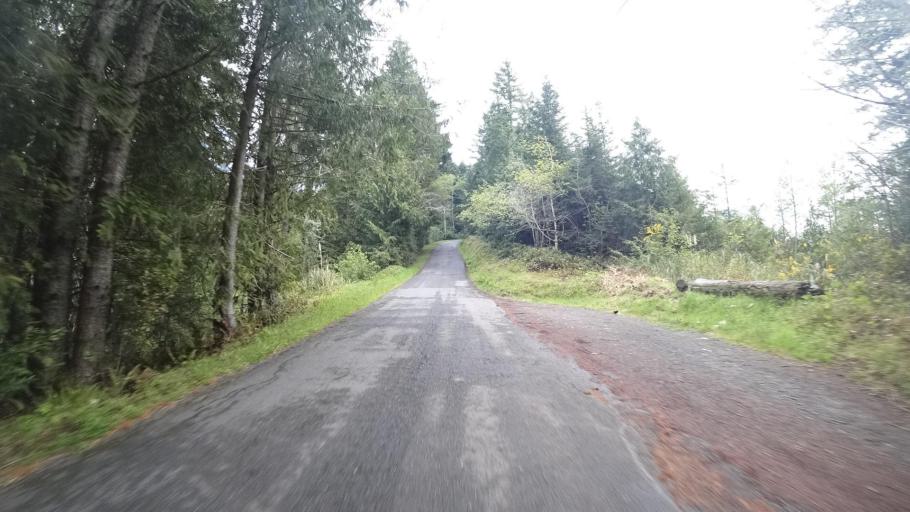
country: US
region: California
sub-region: Humboldt County
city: Bayside
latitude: 40.8258
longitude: -124.0088
